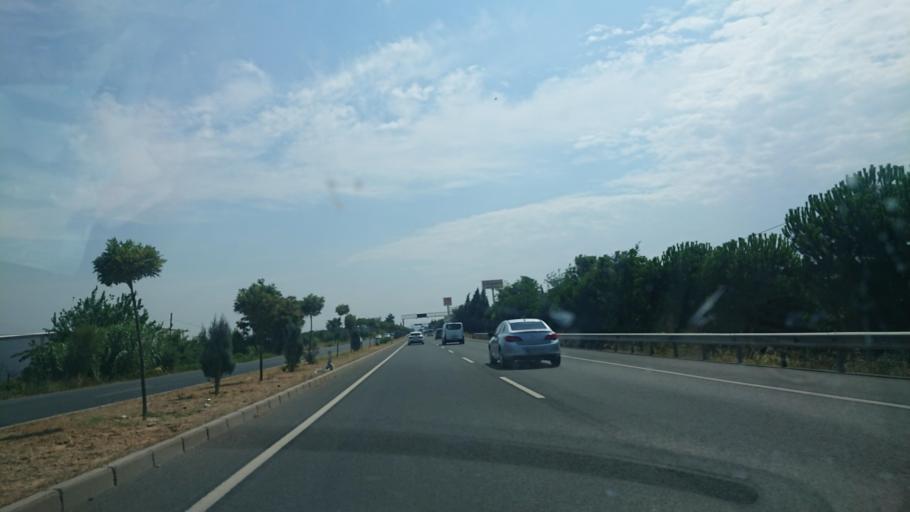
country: TR
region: Manisa
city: Karaoglanli
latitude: 38.4506
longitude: 27.5536
